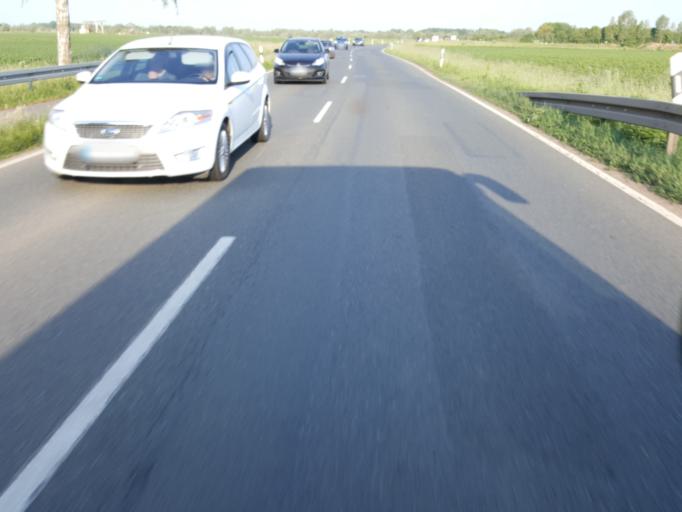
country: DE
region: Lower Saxony
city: Leese
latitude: 52.5078
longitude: 9.1057
